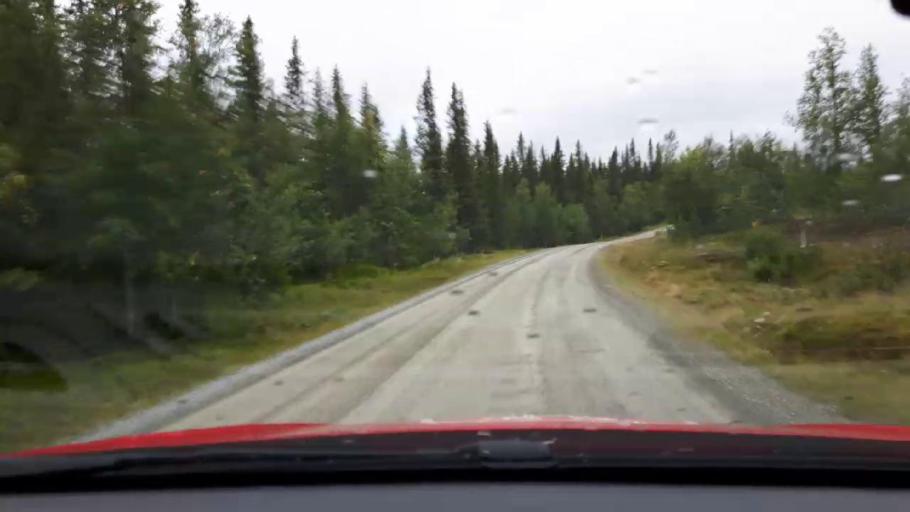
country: SE
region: Jaemtland
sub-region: Bergs Kommun
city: Hoverberg
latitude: 62.8582
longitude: 13.9414
